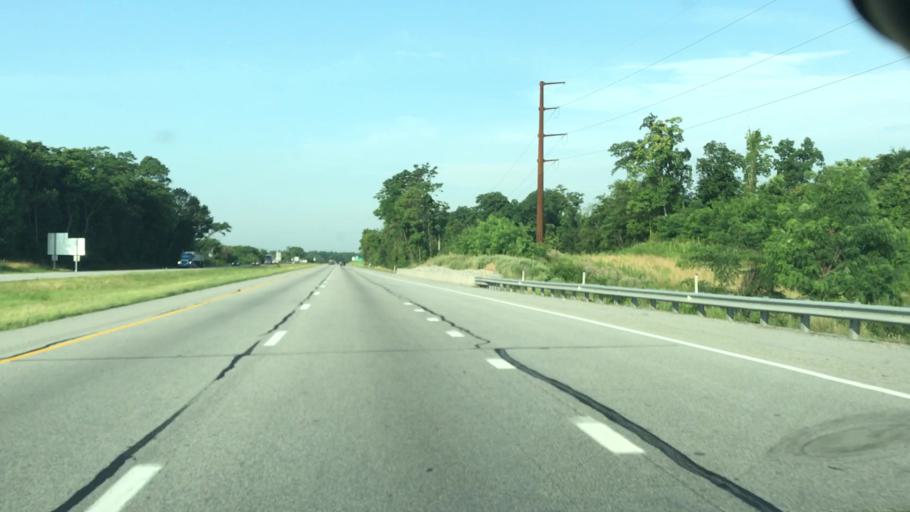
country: US
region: Pennsylvania
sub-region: Cumberland County
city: Carlisle
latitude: 40.1825
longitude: -77.2448
